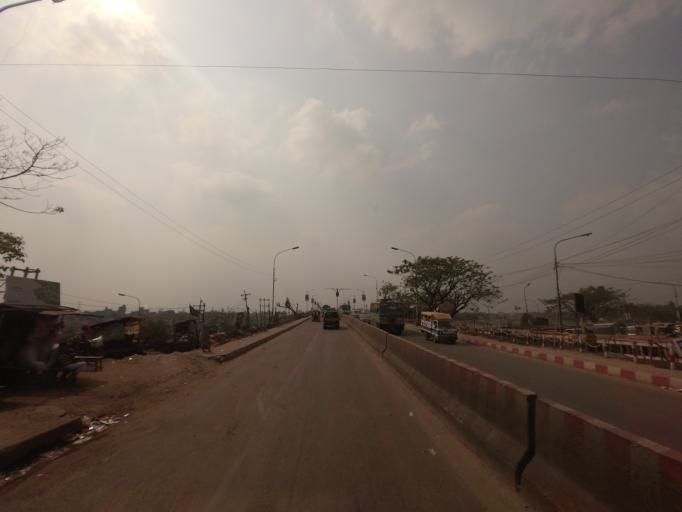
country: BD
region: Dhaka
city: Azimpur
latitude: 23.7836
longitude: 90.3371
